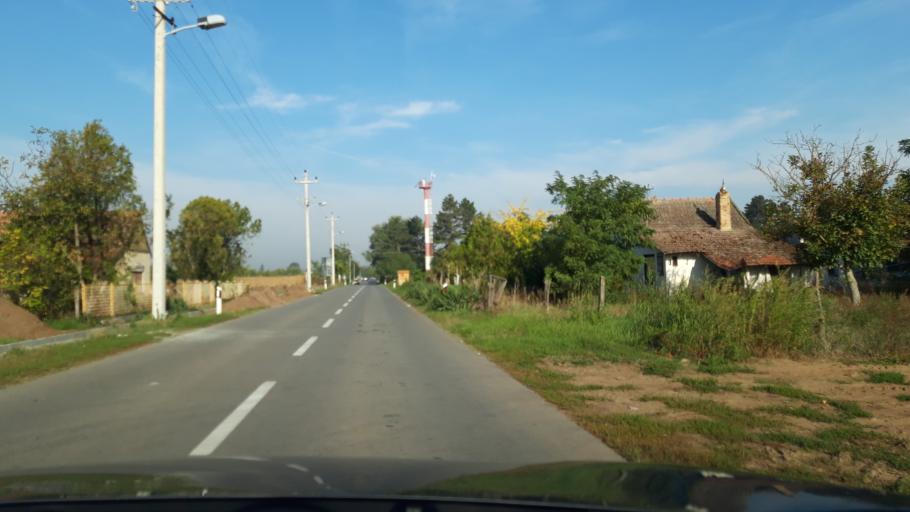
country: HU
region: Csongrad
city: Morahalom
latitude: 46.1397
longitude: 19.8480
